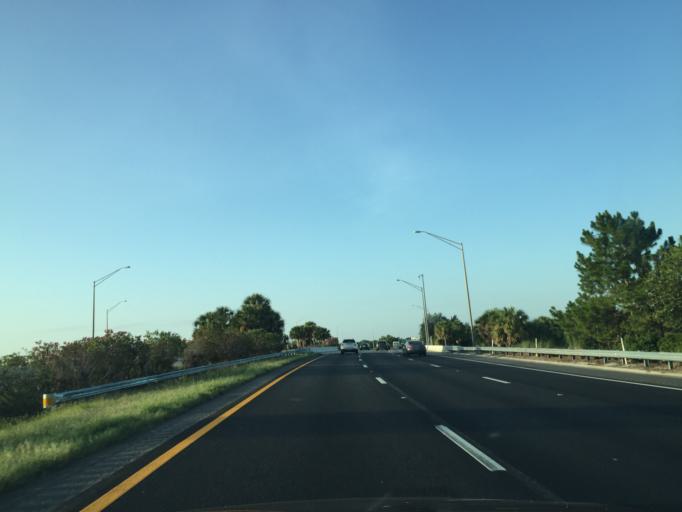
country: US
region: Florida
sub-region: Seminole County
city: Goldenrod
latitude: 28.5985
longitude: -81.2502
